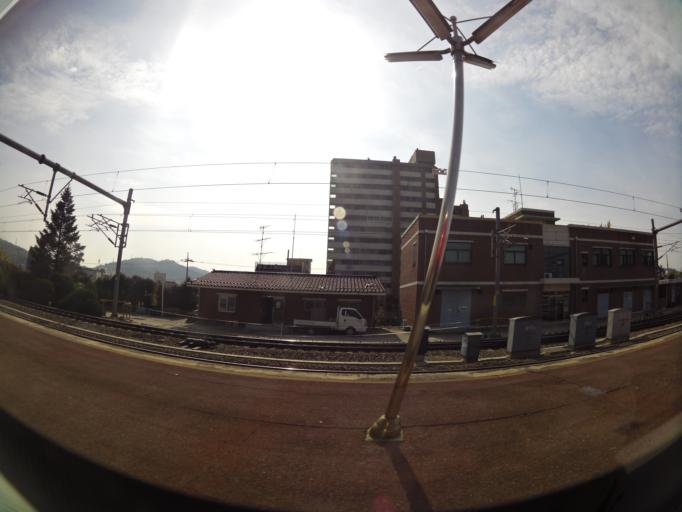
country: KR
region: Daejeon
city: Sintansin
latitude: 36.5321
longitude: 127.3667
